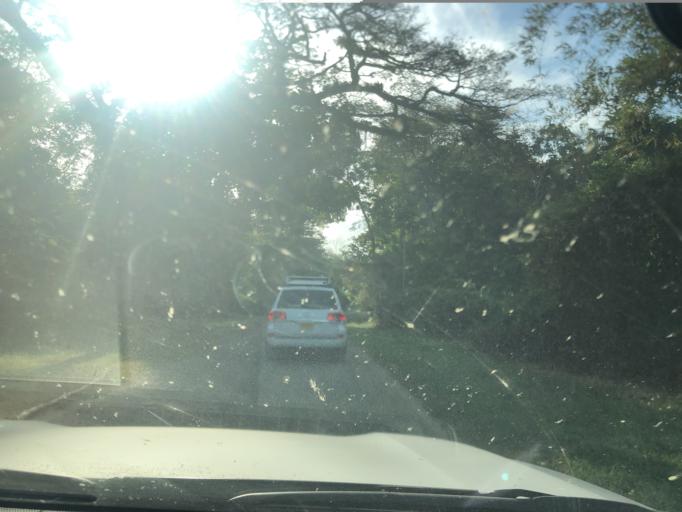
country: NI
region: Rivas
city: Cardenas
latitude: 11.1261
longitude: -85.2965
